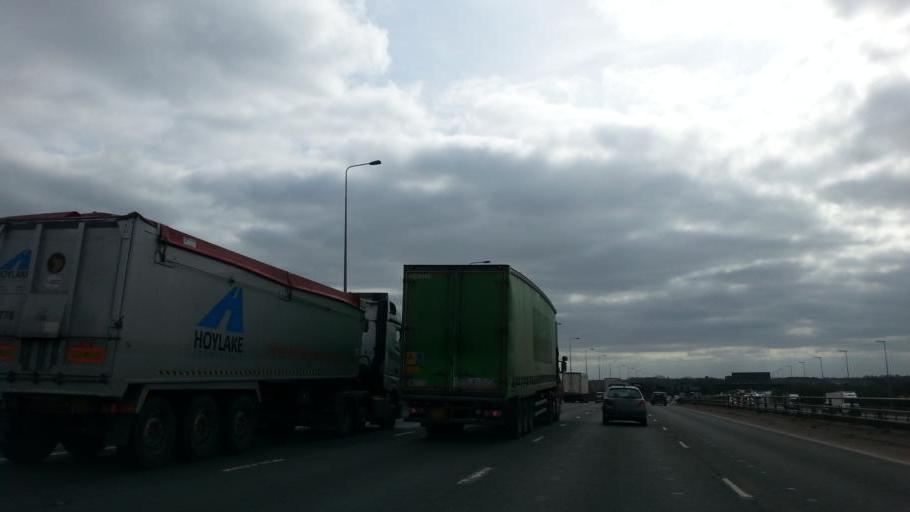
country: GB
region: England
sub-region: Warrington
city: Lymm
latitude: 53.3887
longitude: -2.5051
